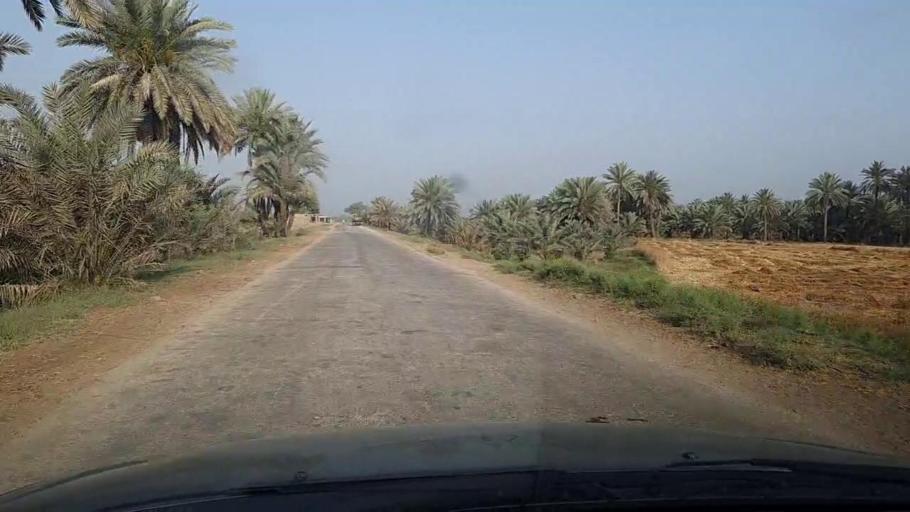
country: PK
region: Sindh
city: Pir jo Goth
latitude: 27.5645
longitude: 68.6478
